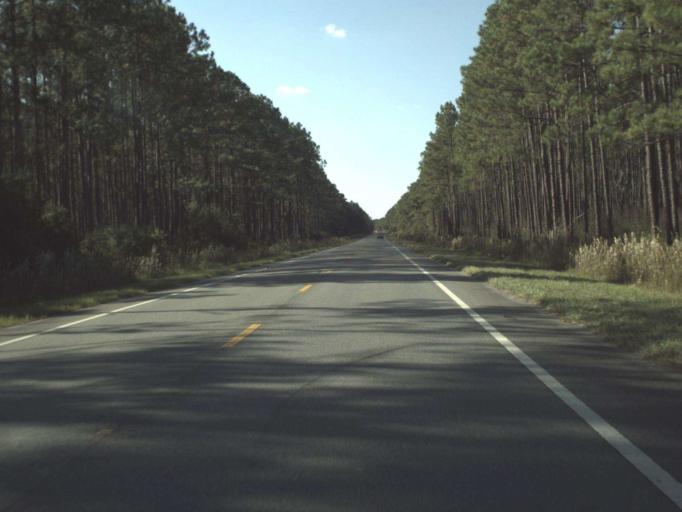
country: US
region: Florida
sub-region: Wakulla County
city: Crawfordville
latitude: 30.3174
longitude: -84.4456
